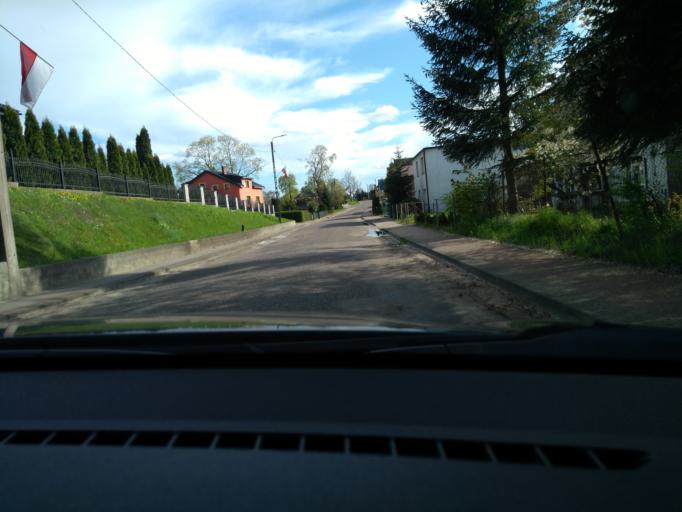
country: PL
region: Pomeranian Voivodeship
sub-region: Powiat leborski
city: Cewice
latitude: 54.3383
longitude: 17.6853
